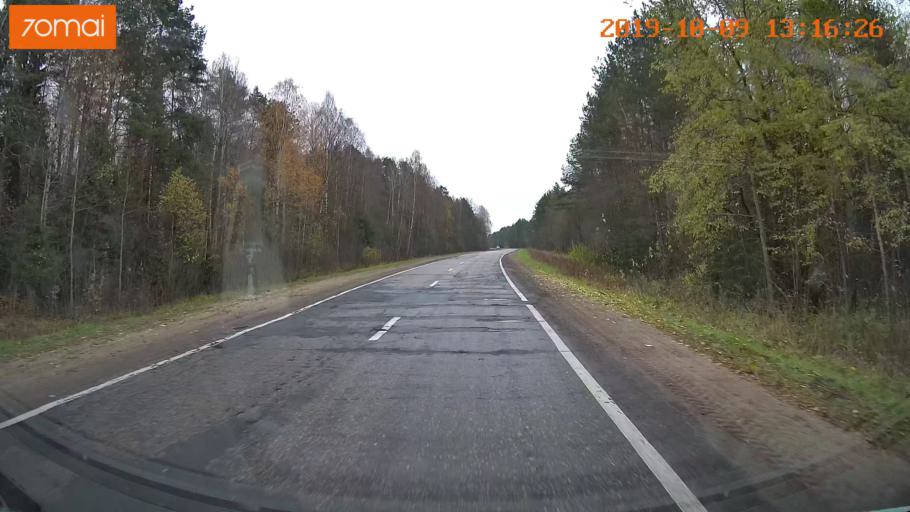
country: RU
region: Jaroslavl
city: Lyubim
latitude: 58.3613
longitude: 40.7657
